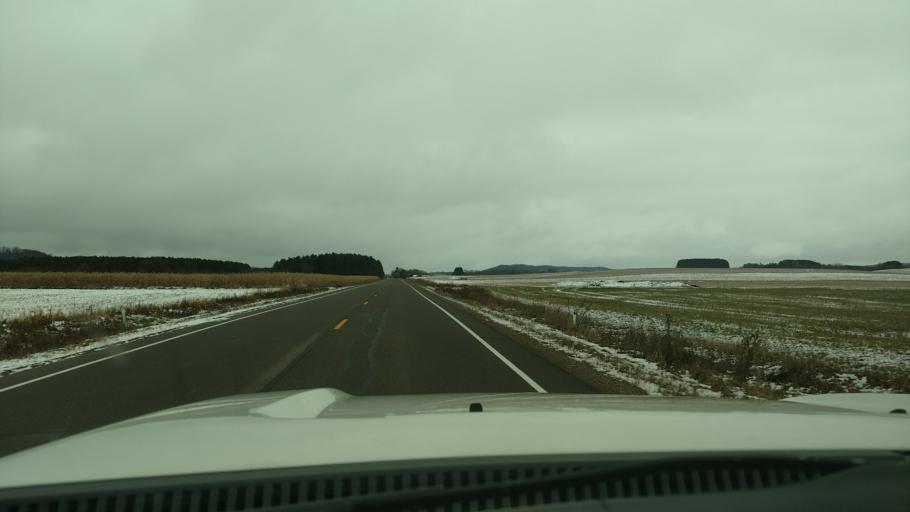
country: US
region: Wisconsin
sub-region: Dunn County
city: Colfax
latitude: 45.1426
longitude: -91.6780
